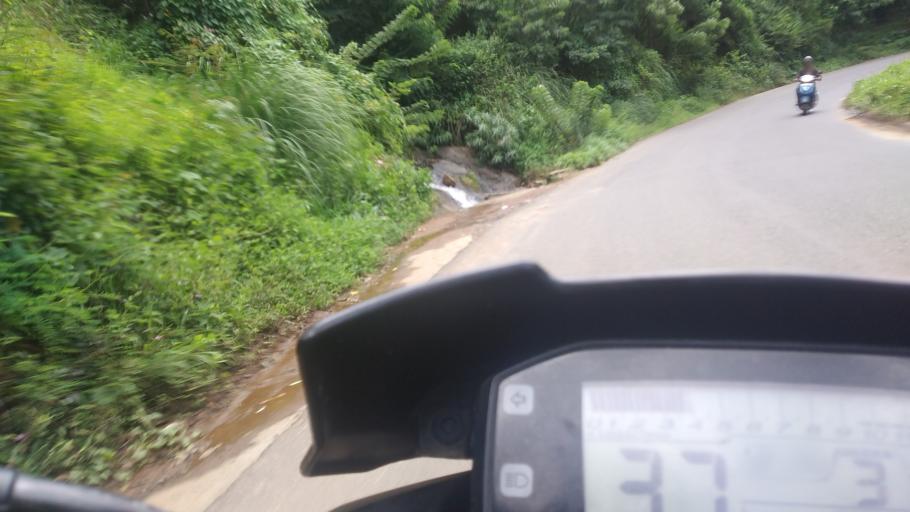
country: IN
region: Kerala
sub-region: Idukki
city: Munnar
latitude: 10.0169
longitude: 77.0027
